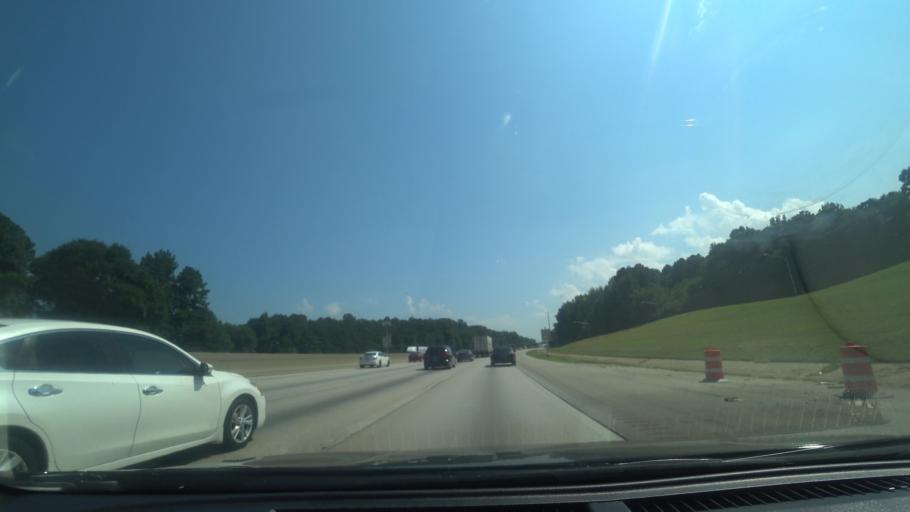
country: US
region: Georgia
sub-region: DeKalb County
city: Avondale Estates
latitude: 33.7690
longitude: -84.2328
